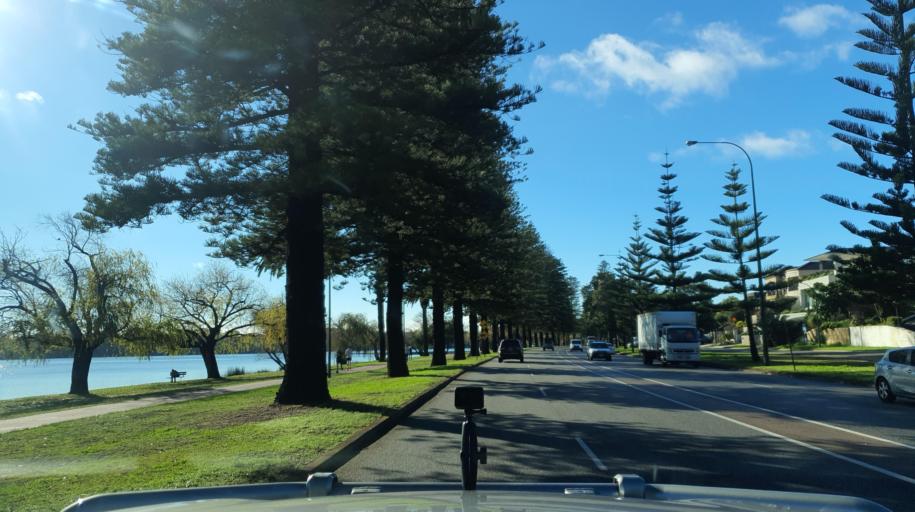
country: AU
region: Western Australia
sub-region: Cambridge
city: West Leederville
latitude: -31.9334
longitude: 115.8258
